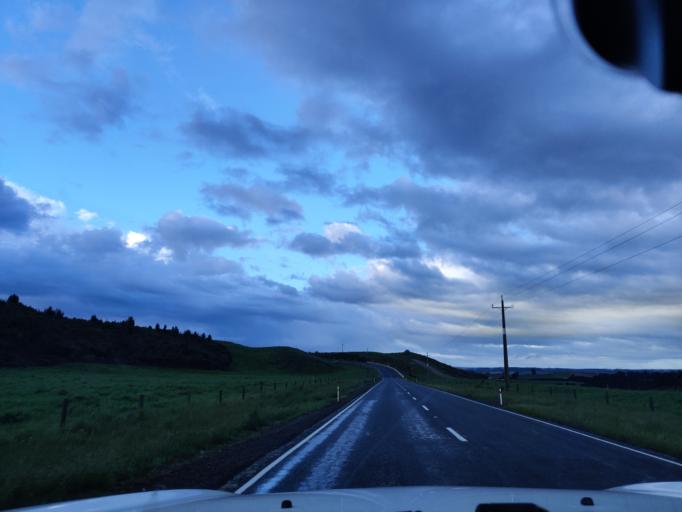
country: NZ
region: Waikato
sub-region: South Waikato District
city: Tokoroa
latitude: -38.3833
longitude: 175.7842
